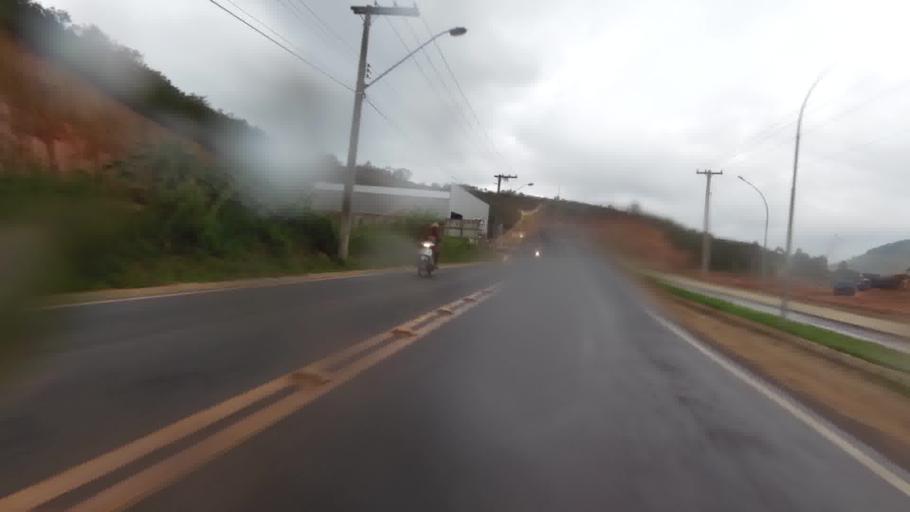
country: BR
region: Espirito Santo
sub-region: Alfredo Chaves
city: Alfredo Chaves
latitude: -20.6419
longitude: -40.7467
